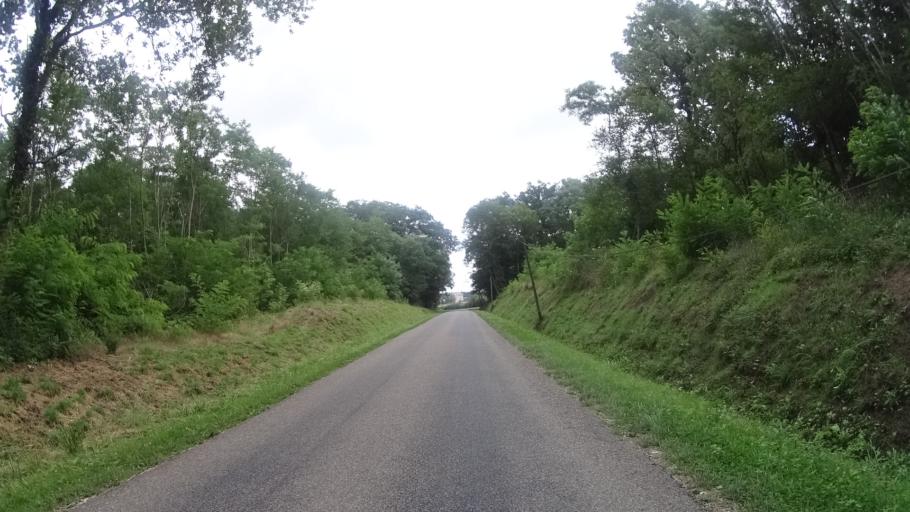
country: FR
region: Champagne-Ardenne
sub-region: Departement de l'Aube
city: Ervy-le-Chatel
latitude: 48.0718
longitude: 3.9545
